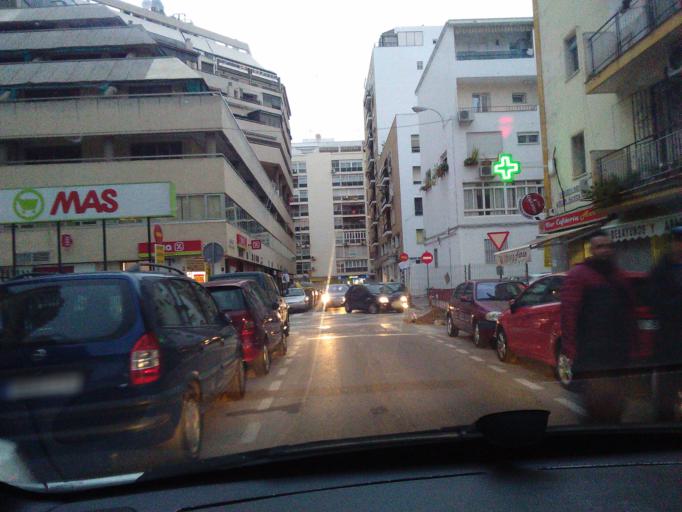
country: ES
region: Andalusia
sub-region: Provincia de Sevilla
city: Sevilla
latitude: 37.3756
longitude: -6.0042
